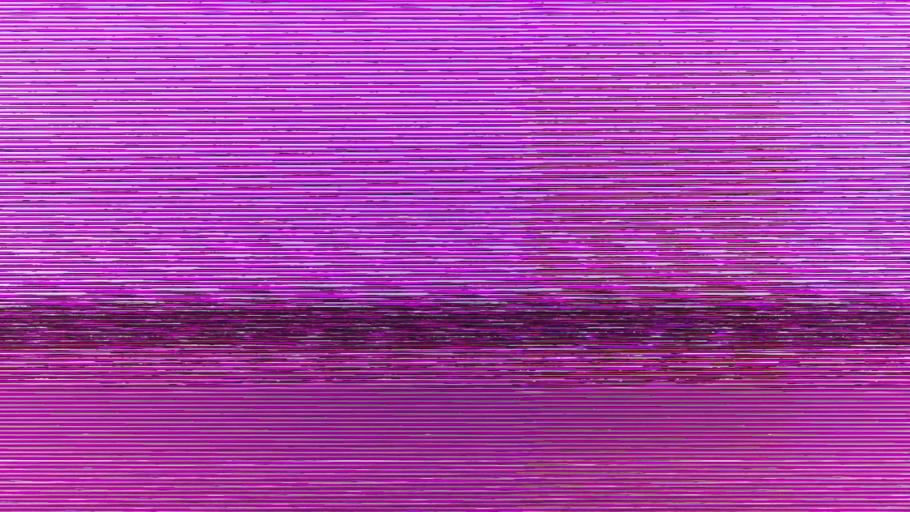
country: US
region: Michigan
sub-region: Genesee County
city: Swartz Creek
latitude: 43.0013
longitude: -83.8118
